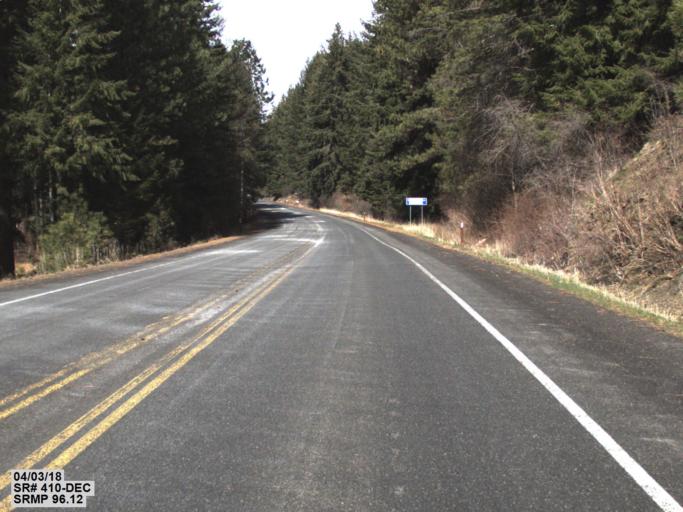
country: US
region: Washington
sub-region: Kittitas County
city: Cle Elum
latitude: 46.9421
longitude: -121.0640
